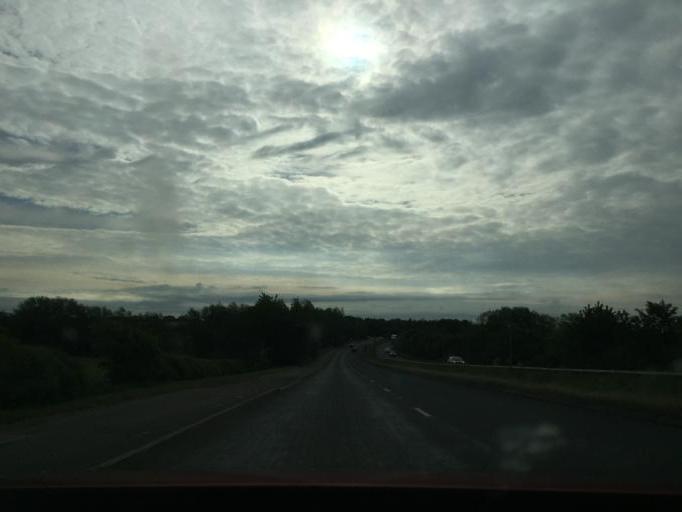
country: GB
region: England
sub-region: Leicestershire
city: Lutterworth
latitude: 52.4533
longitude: -1.2302
